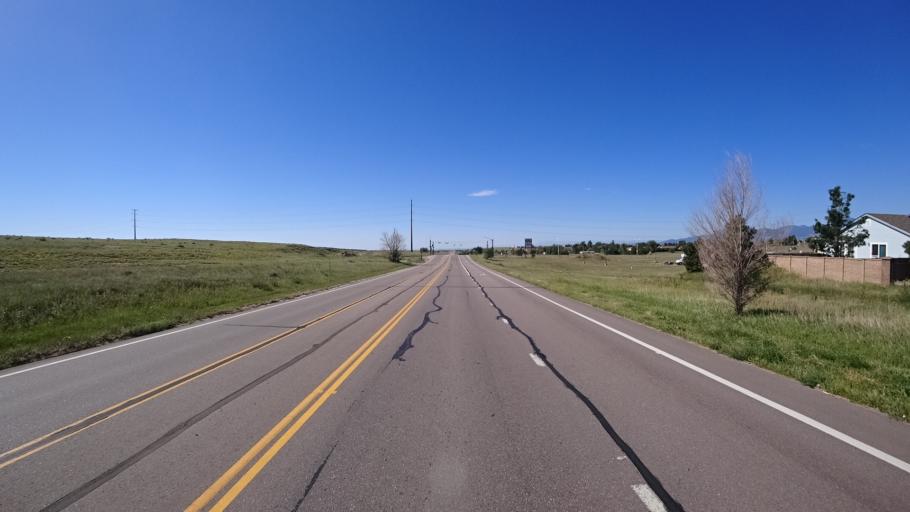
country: US
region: Colorado
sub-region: El Paso County
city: Cimarron Hills
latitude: 38.9027
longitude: -104.6829
